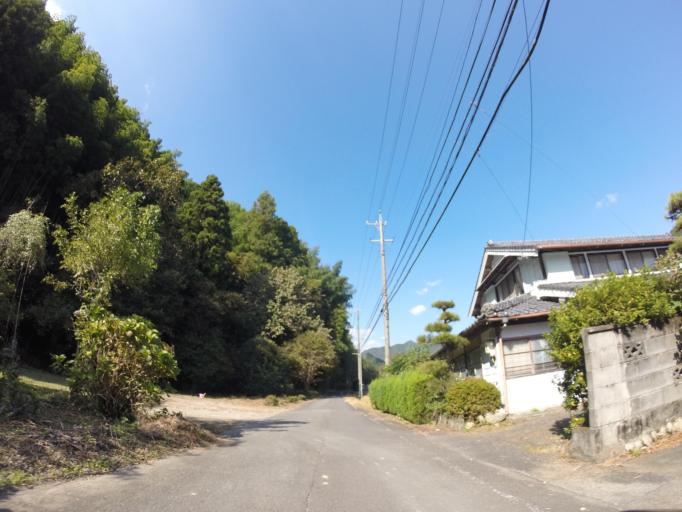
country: JP
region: Shizuoka
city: Shizuoka-shi
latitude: 35.1144
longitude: 138.4588
